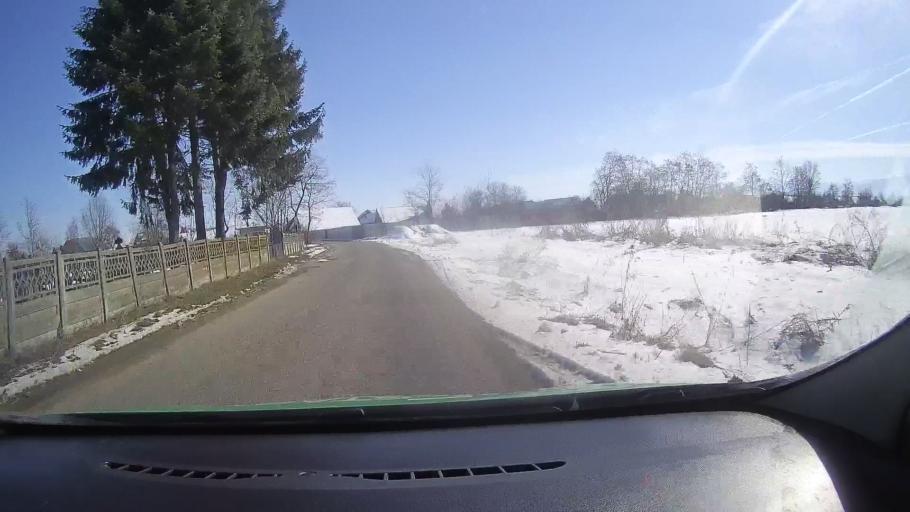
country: RO
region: Brasov
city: Fogarasch
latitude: 45.8159
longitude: 25.0008
